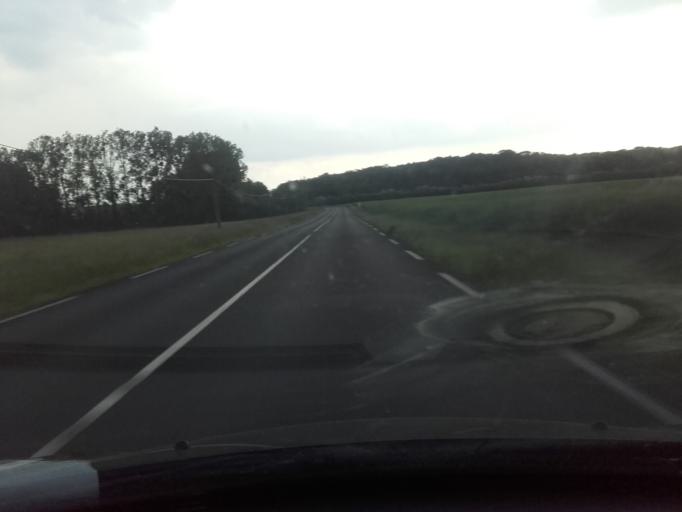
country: FR
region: Centre
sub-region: Departement d'Indre-et-Loire
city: Auzouer-en-Touraine
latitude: 47.5310
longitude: 0.9892
